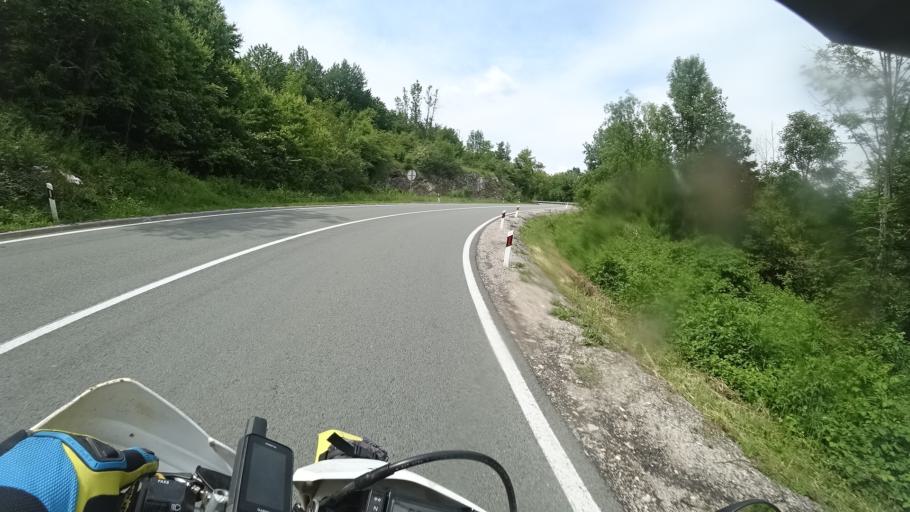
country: BA
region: Federation of Bosnia and Herzegovina
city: Izacic
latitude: 44.8793
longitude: 15.7034
